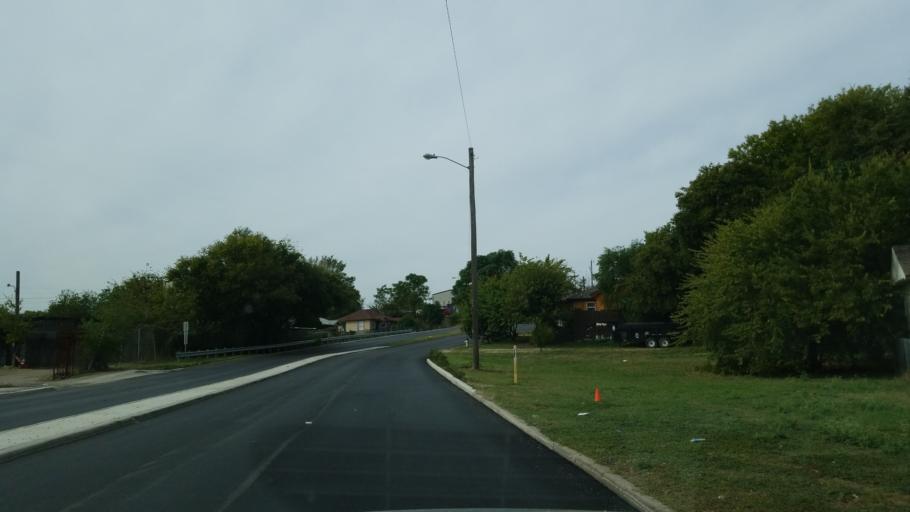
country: US
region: Texas
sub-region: Dallas County
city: Dallas
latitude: 32.7834
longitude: -96.7349
